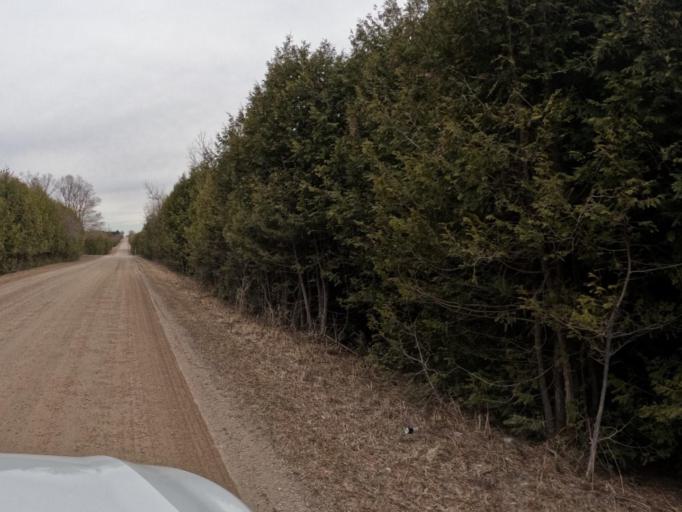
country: CA
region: Ontario
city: Orangeville
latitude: 43.9262
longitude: -80.2568
